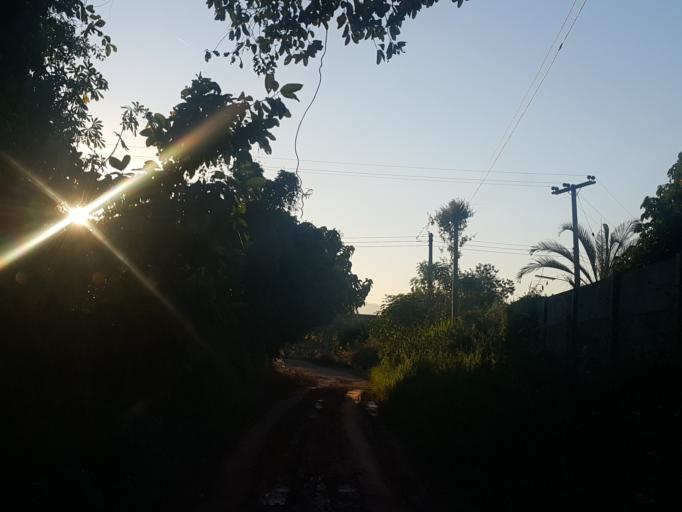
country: TH
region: Chiang Mai
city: San Sai
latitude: 18.8646
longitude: 99.1442
